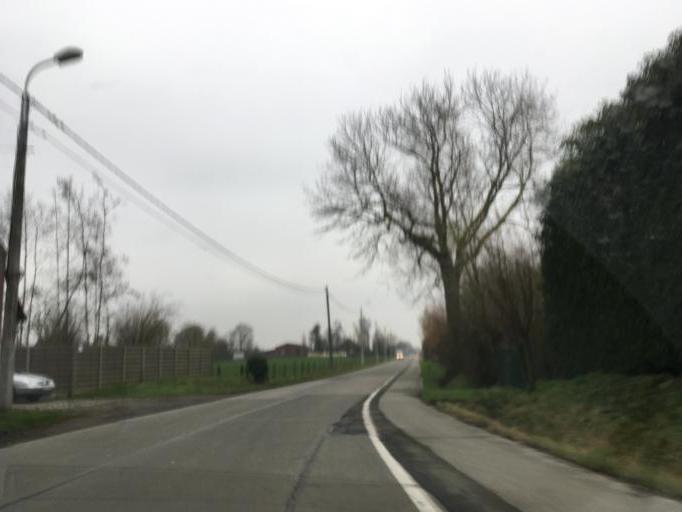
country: BE
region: Flanders
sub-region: Provincie West-Vlaanderen
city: Ledegem
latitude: 50.8924
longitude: 3.1633
